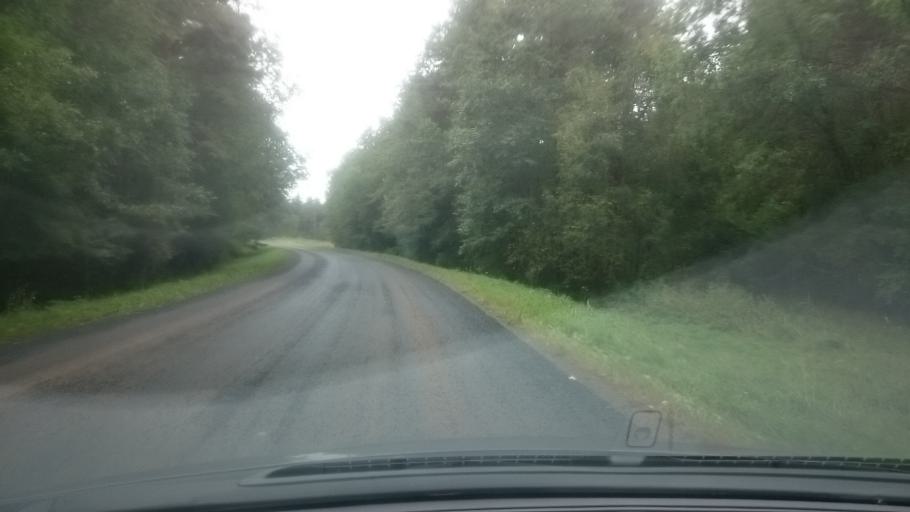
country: EE
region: Harju
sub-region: Raasiku vald
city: Raasiku
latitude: 59.4692
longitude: 25.2414
